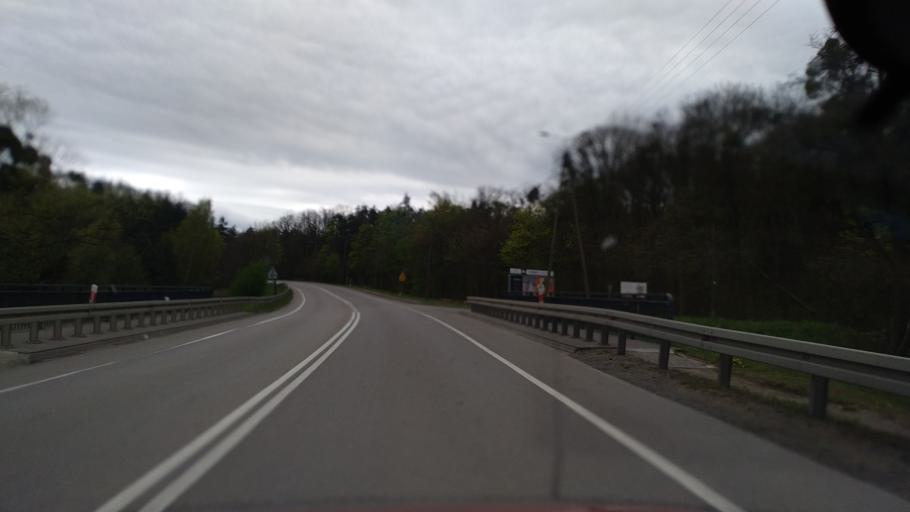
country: PL
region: Pomeranian Voivodeship
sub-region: Powiat starogardzki
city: Starogard Gdanski
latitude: 53.9720
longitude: 18.5535
